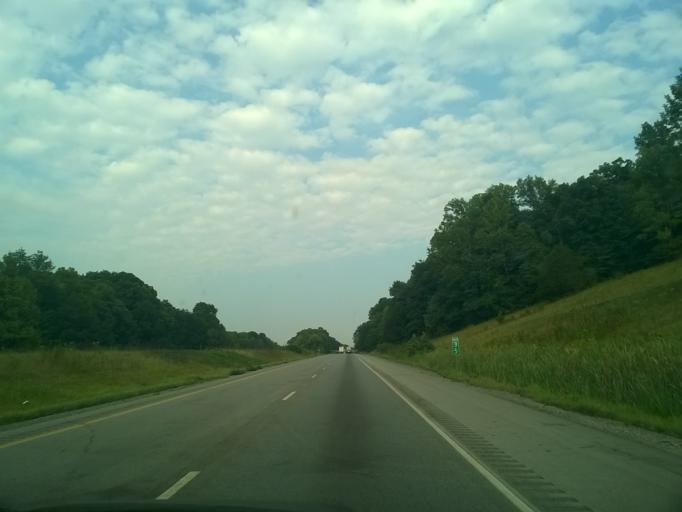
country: US
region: Indiana
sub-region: Putnam County
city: Cloverdale
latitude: 39.5161
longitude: -86.9126
